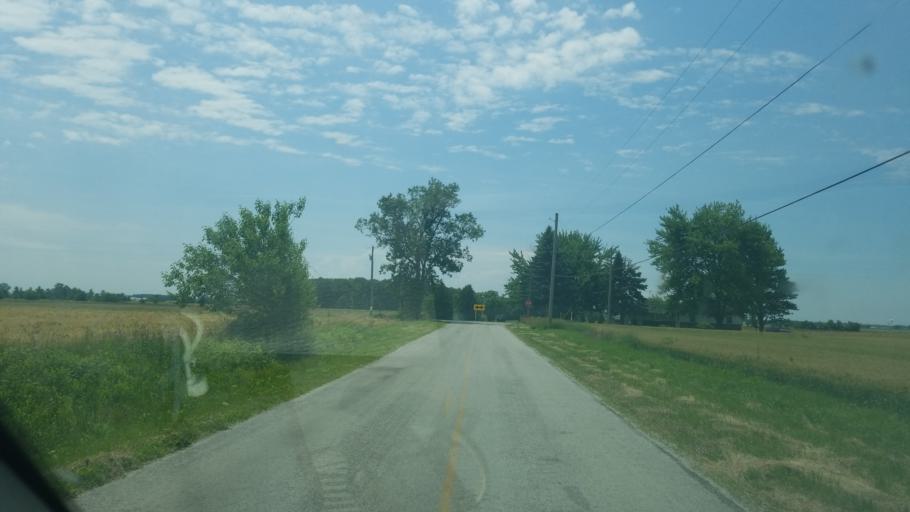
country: US
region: Ohio
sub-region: Wood County
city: North Baltimore
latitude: 41.2229
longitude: -83.6212
